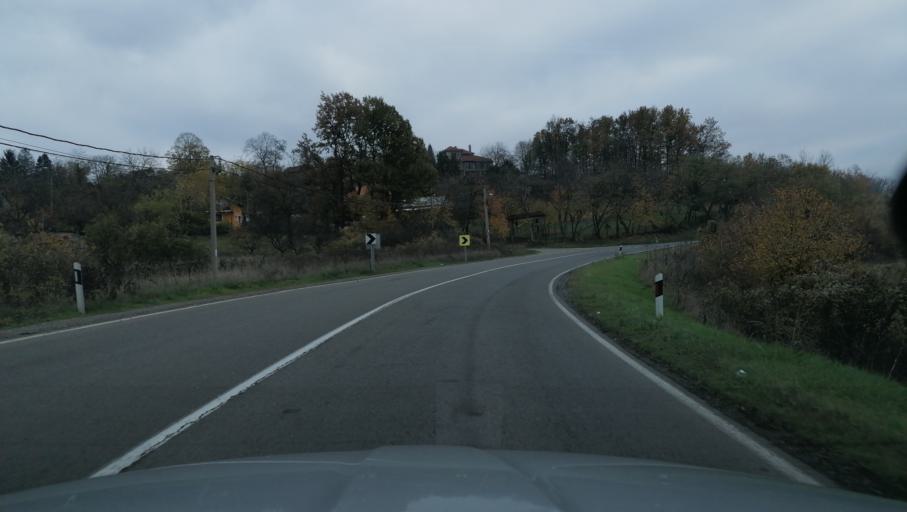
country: RS
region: Central Serbia
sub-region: Belgrade
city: Grocka
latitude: 44.7123
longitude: 20.6611
